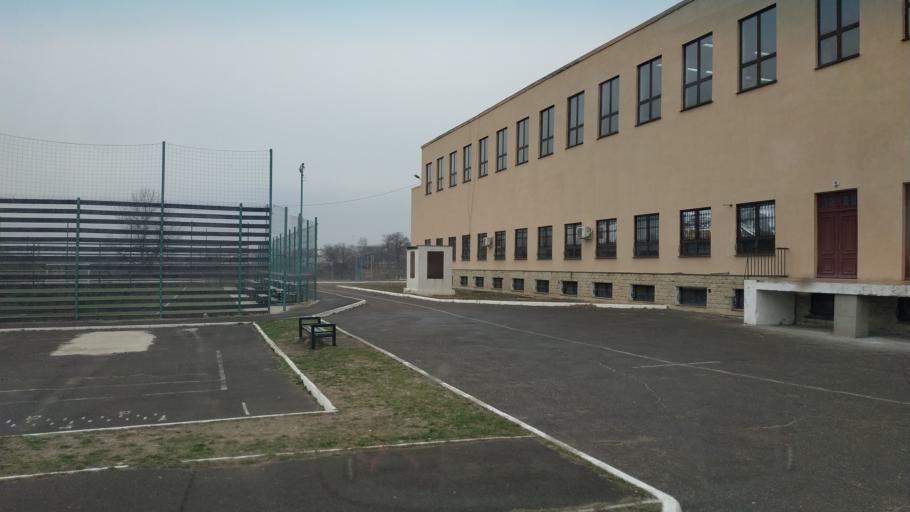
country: MD
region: Chisinau
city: Singera
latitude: 46.9138
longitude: 28.9747
